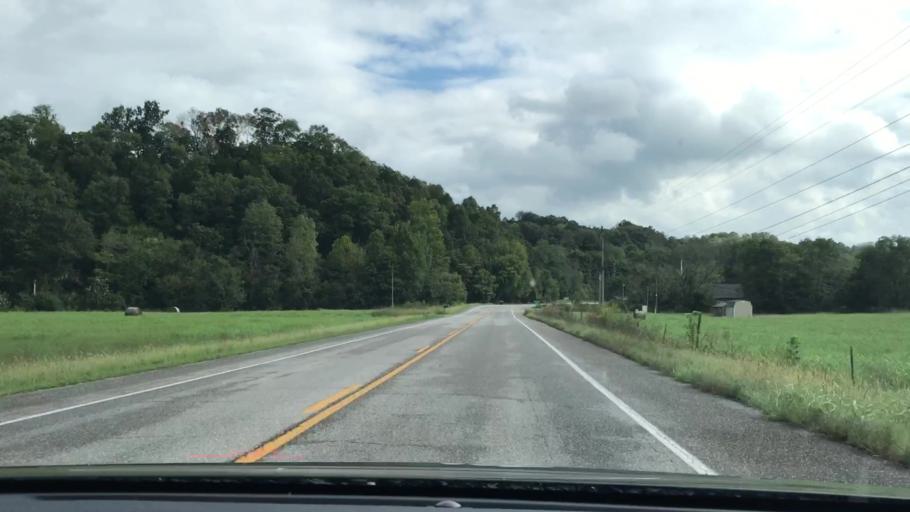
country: US
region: Kentucky
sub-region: Metcalfe County
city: Edmonton
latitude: 36.8469
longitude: -85.6118
